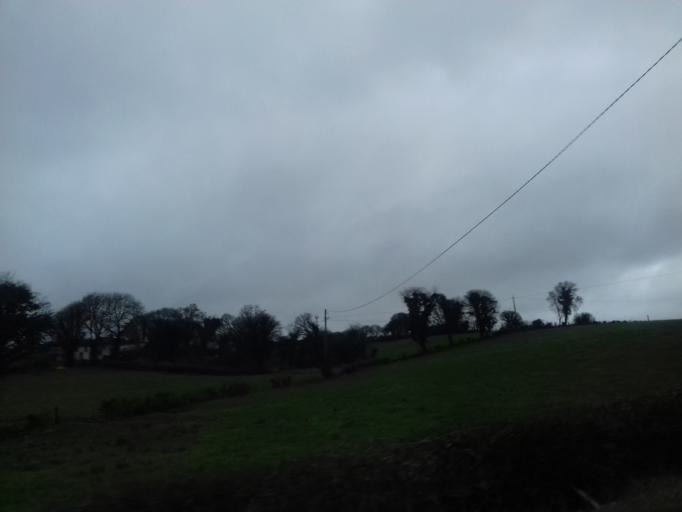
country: IE
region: Ulster
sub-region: County Monaghan
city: Castleblayney
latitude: 54.0701
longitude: -6.6870
